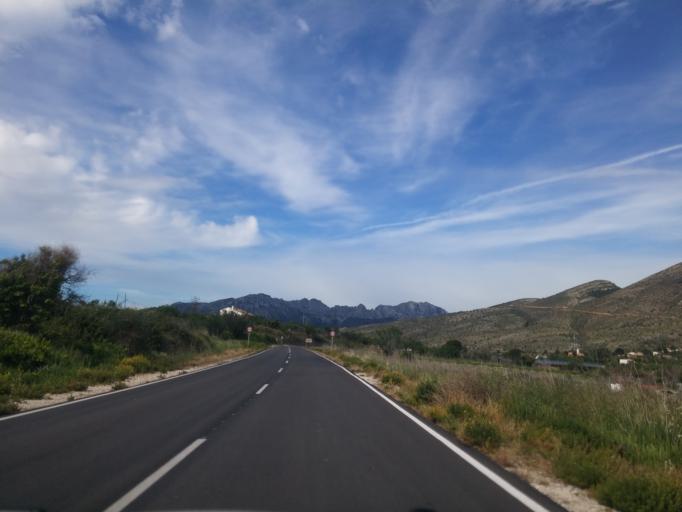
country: ES
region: Valencia
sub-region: Provincia de Alicante
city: Benissa
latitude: 38.7078
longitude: 0.0286
